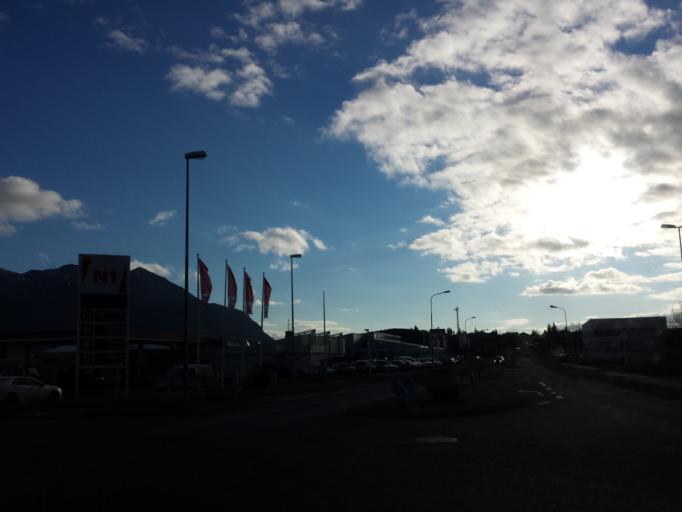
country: IS
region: West
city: Borgarnes
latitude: 64.5446
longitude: -21.9106
